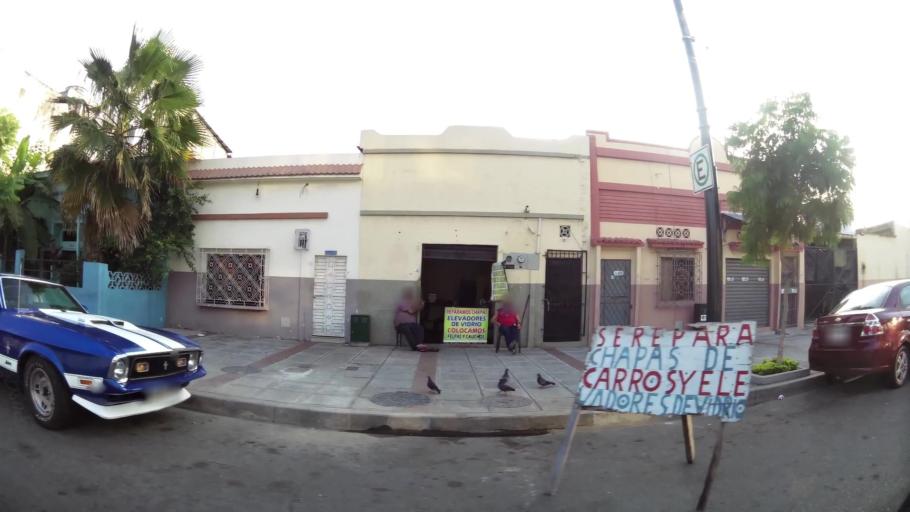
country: EC
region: Guayas
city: Guayaquil
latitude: -2.2112
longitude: -79.9001
